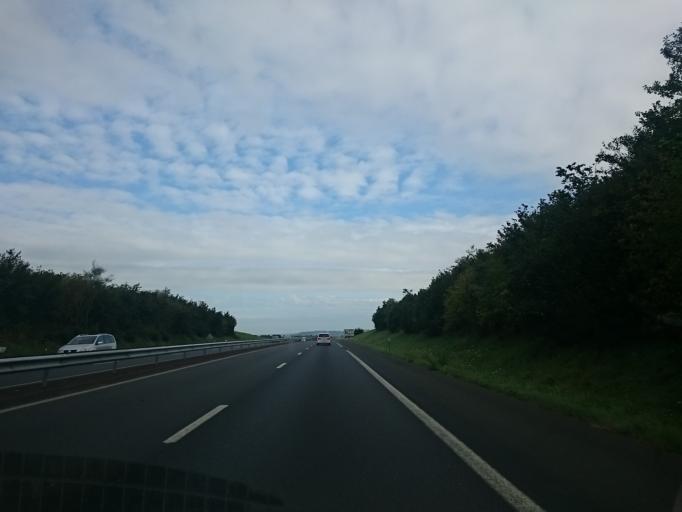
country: FR
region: Lower Normandy
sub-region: Departement de la Manche
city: Ducey
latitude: 48.6024
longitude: -1.3319
